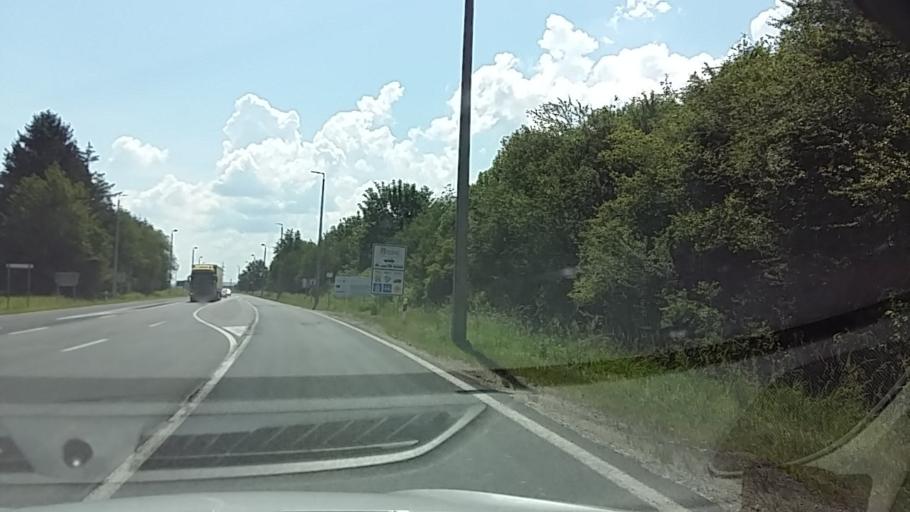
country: AT
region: Burgenland
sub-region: Politischer Bezirk Jennersdorf
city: Heiligenkreuz im Lafnitztal
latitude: 46.9798
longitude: 16.2841
